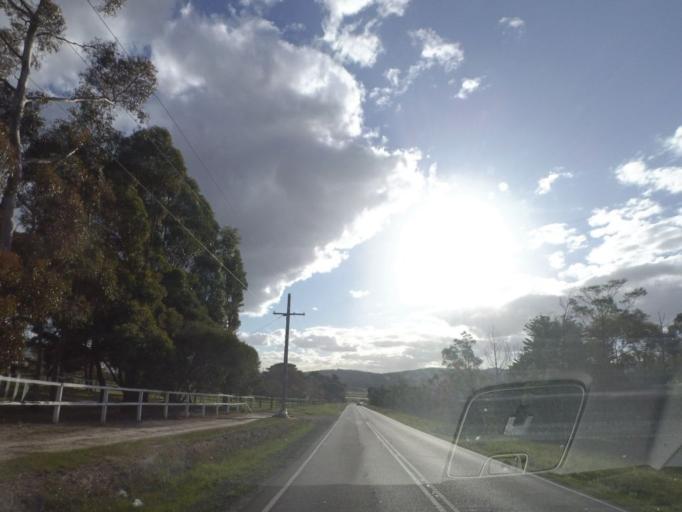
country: AU
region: Victoria
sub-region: Yarra Ranges
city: Yarra Glen
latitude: -37.6957
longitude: 145.3498
